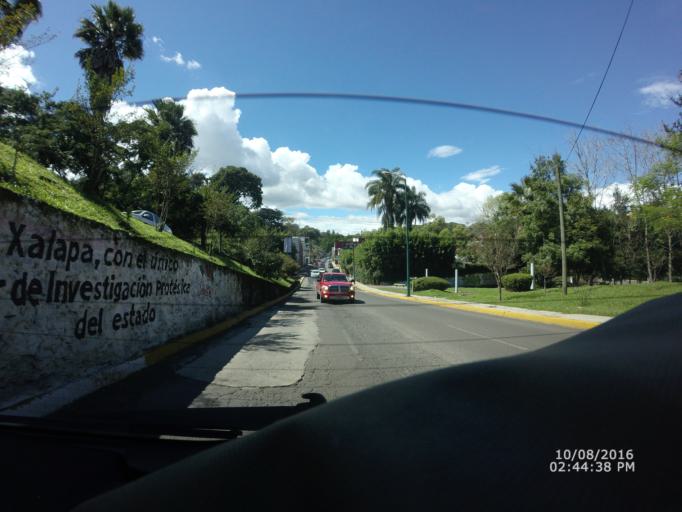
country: MX
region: Veracruz
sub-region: Xalapa
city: Lomas Verdes
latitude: 19.5075
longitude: -96.9003
